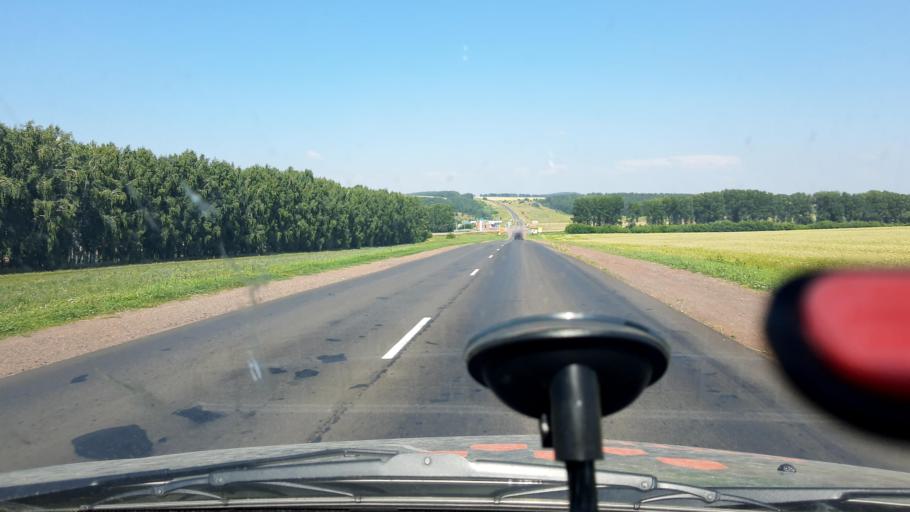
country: RU
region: Bashkortostan
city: Chekmagush
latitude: 55.1266
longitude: 54.6784
